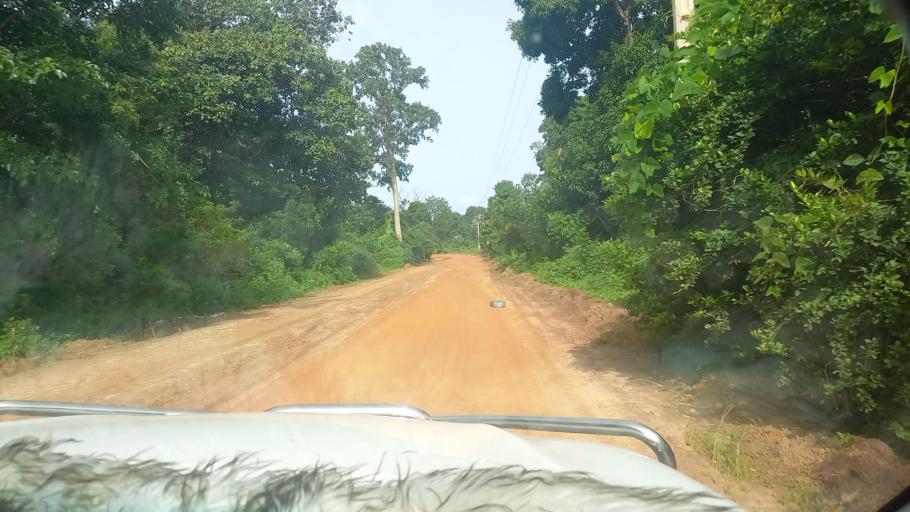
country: SN
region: Ziguinchor
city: Ziguinchor
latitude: 12.6691
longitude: -16.2693
